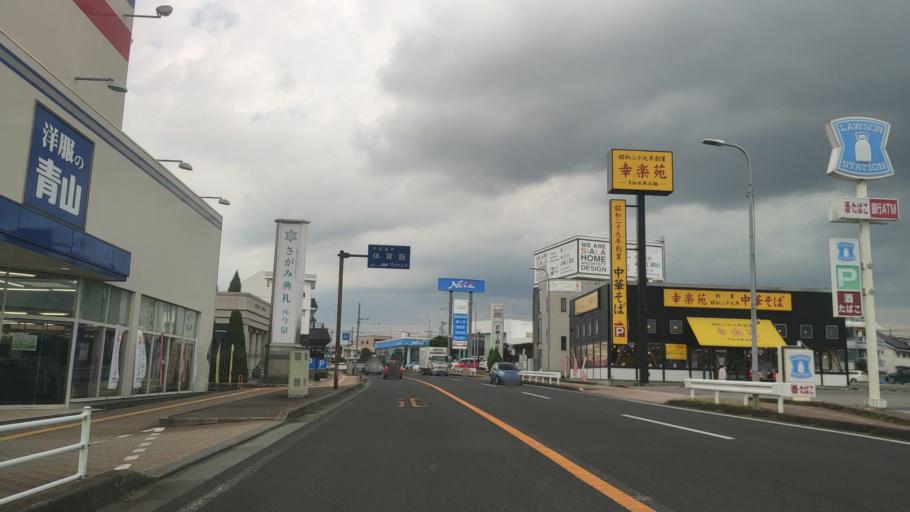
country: JP
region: Tochigi
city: Utsunomiya-shi
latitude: 36.5612
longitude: 139.9150
